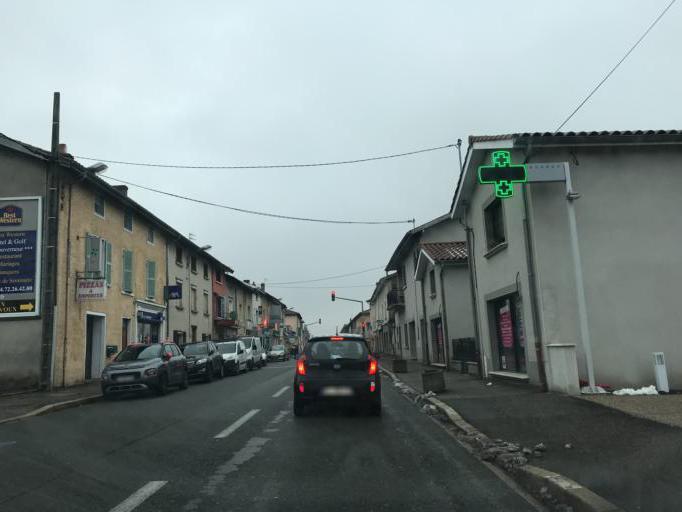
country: FR
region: Rhone-Alpes
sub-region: Departement de l'Ain
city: Villars-les-Dombes
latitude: 46.0007
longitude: 5.0302
